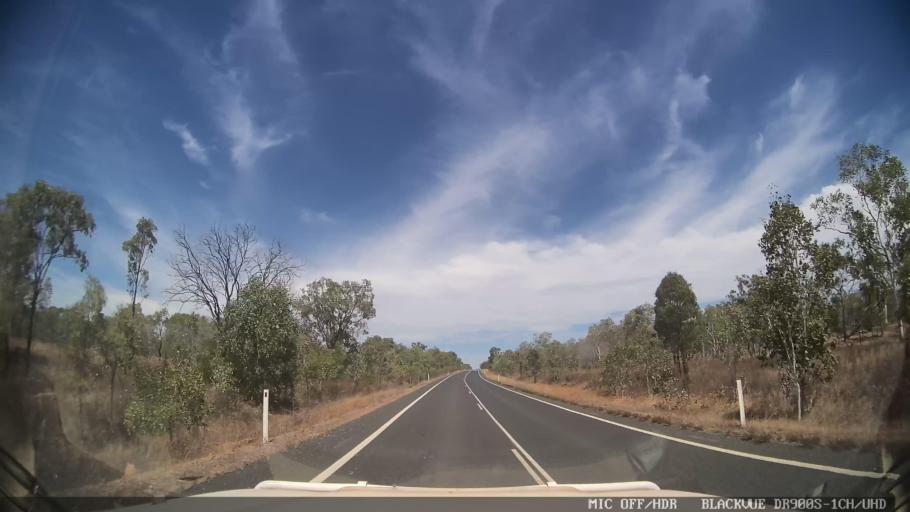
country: AU
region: Queensland
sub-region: Cook
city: Cooktown
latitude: -15.8770
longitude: 144.8606
